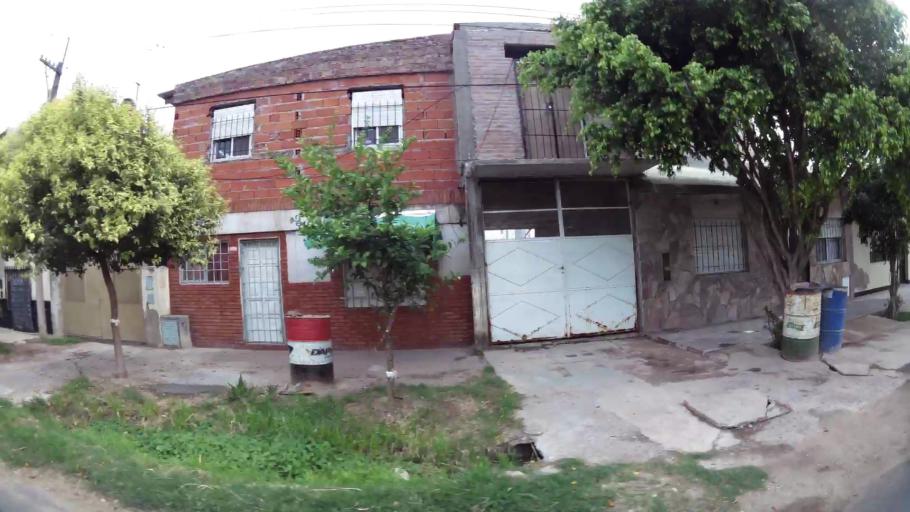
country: AR
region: Santa Fe
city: Gobernador Galvez
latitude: -33.0151
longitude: -60.6475
